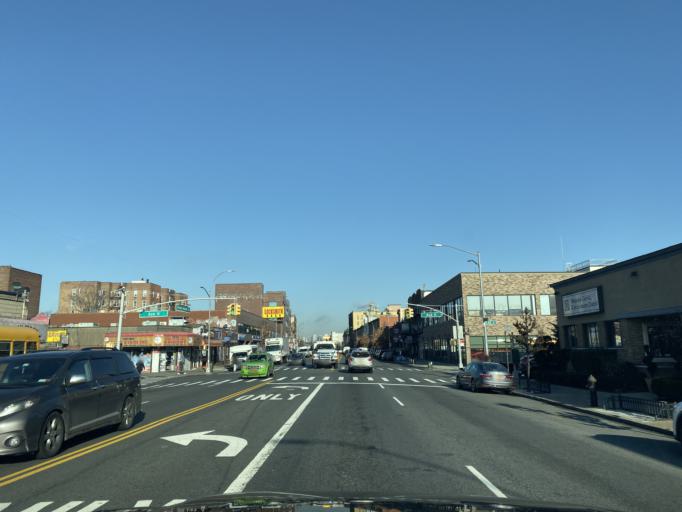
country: US
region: New York
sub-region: Kings County
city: Brooklyn
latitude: 40.6292
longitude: -73.9660
